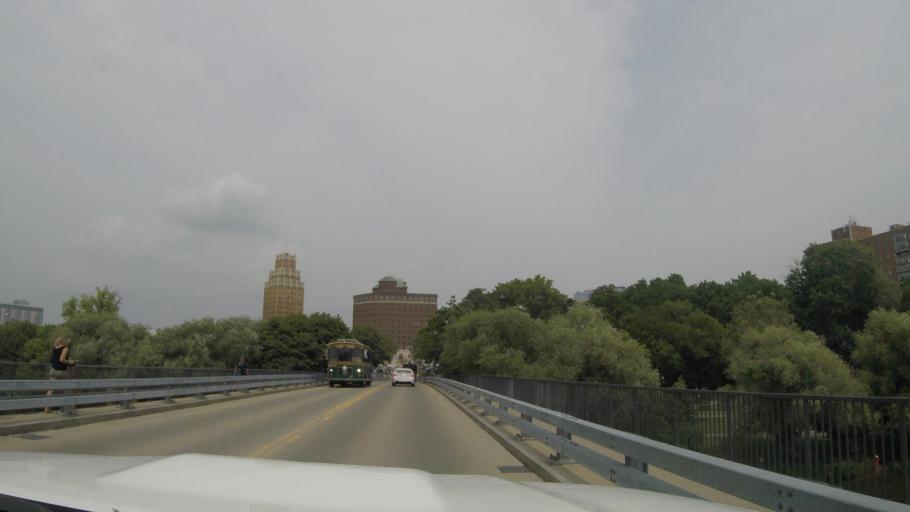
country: US
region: New York
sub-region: Niagara County
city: Niagara Falls
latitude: 43.0825
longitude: -79.0634
